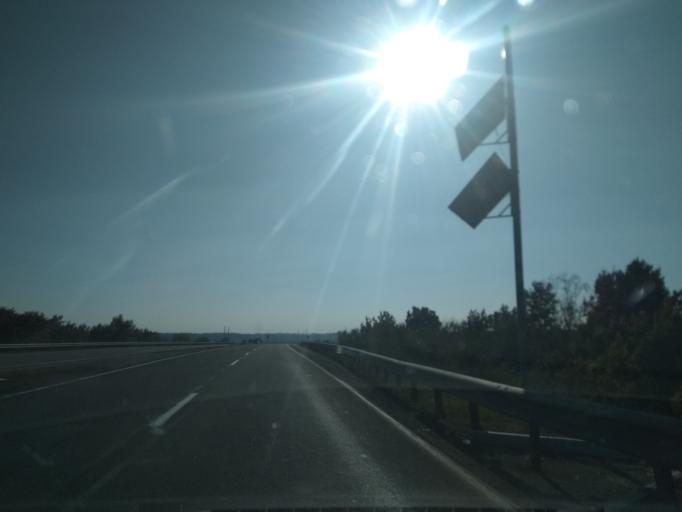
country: BY
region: Brest
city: Horad Kobryn
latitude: 52.2074
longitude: 24.4211
